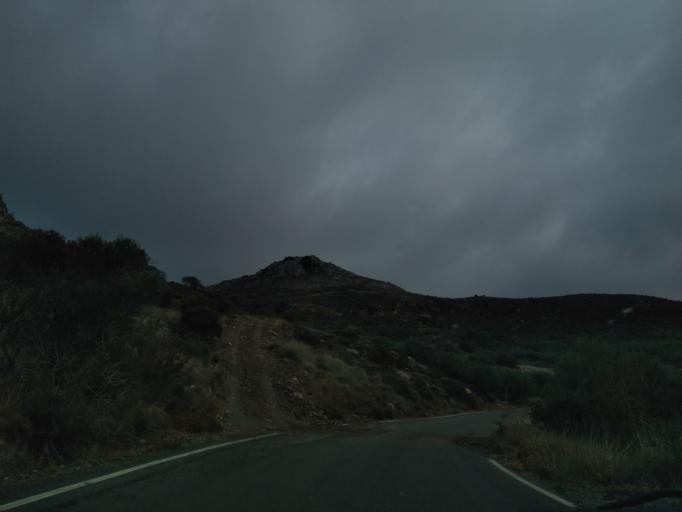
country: GR
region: Crete
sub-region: Nomos Lasithiou
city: Siteia
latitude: 35.1503
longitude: 26.0201
